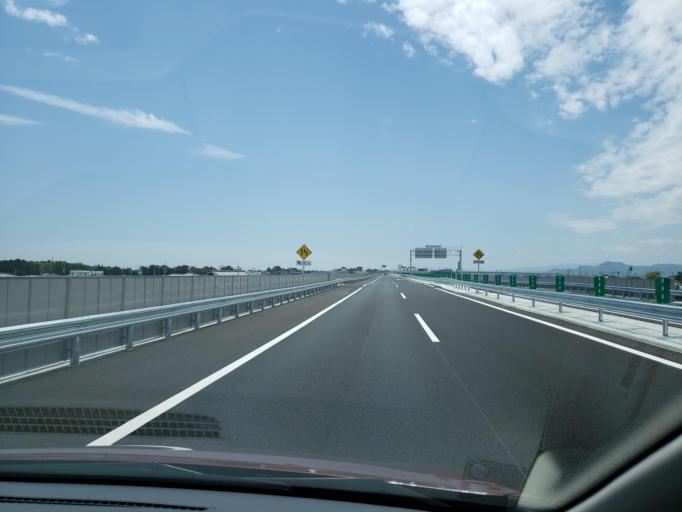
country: JP
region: Tokushima
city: Tokushima-shi
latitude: 34.0948
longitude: 134.5994
